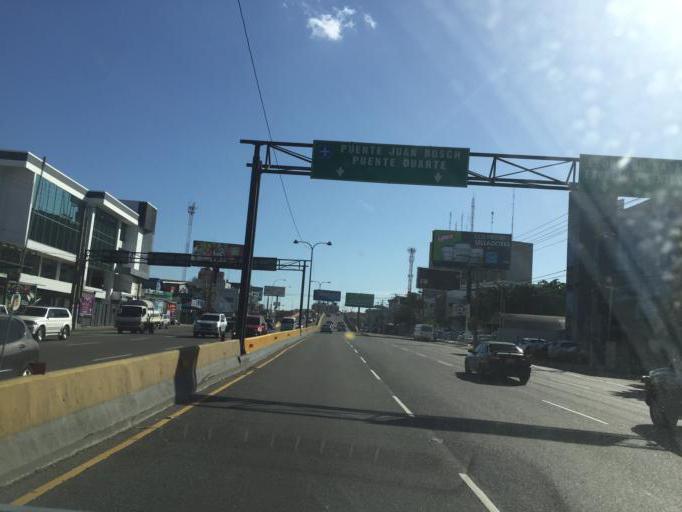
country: DO
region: Nacional
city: San Carlos
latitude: 18.4760
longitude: -69.9099
